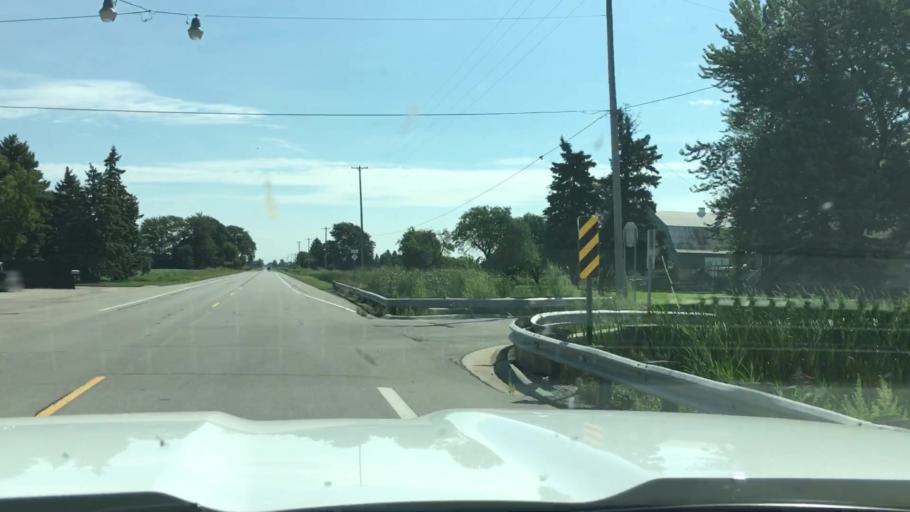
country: US
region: Michigan
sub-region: Bay County
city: Essexville
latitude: 43.5905
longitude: -83.7500
